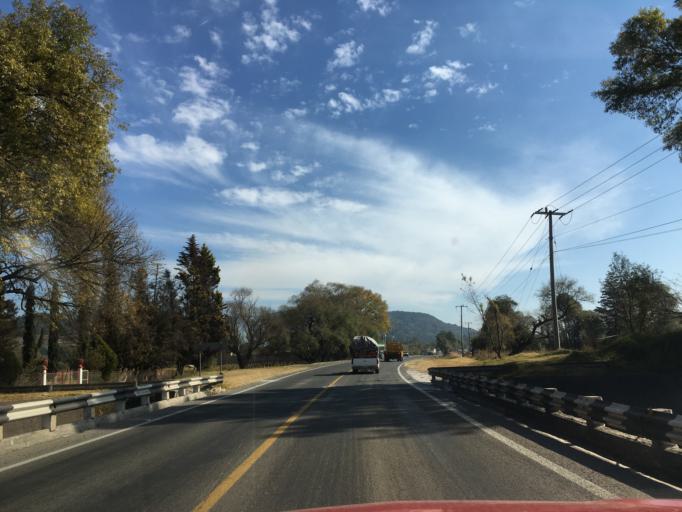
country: MX
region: Michoacan
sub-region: Hidalgo
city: Colonia Ecologica Asociacion de Lucha Social (Lucha Social)
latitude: 19.6973
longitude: -100.6097
